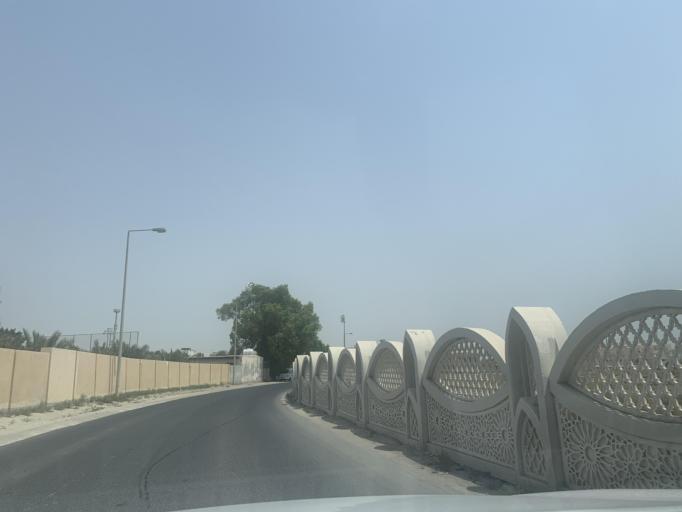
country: BH
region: Manama
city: Jidd Hafs
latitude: 26.2265
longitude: 50.4650
